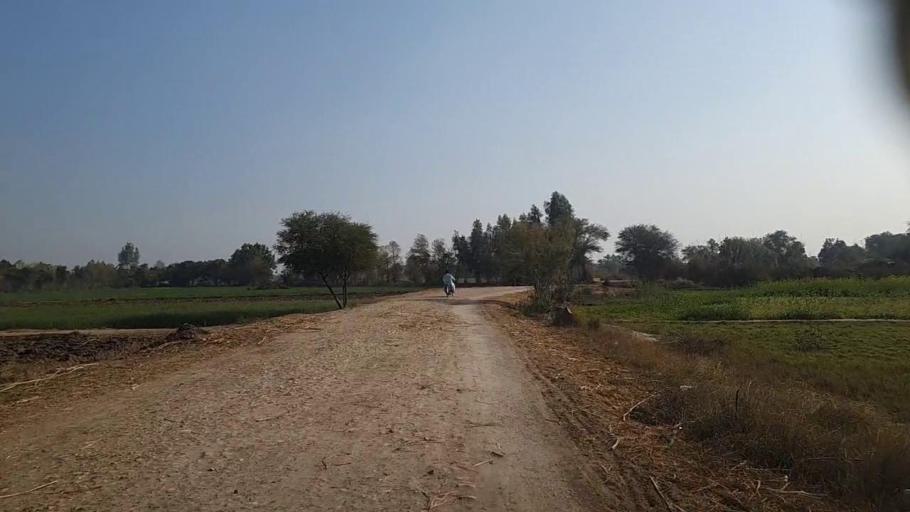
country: PK
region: Sindh
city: Mirpur Mathelo
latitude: 27.8947
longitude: 69.6074
